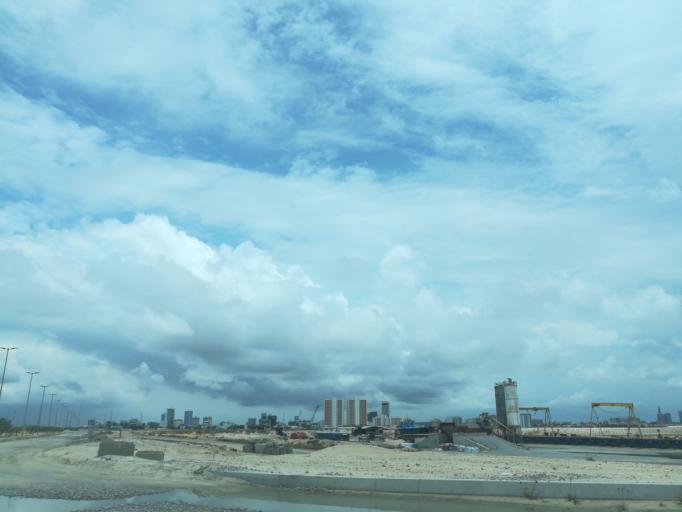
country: NG
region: Lagos
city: Ikoyi
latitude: 6.4089
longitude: 3.4271
